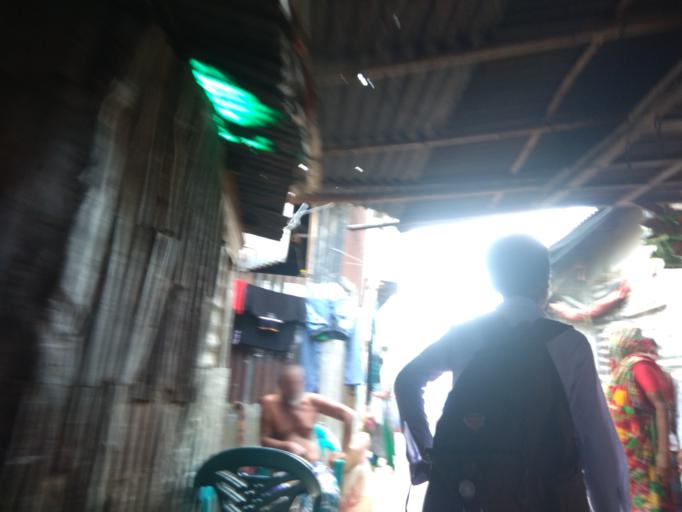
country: BD
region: Dhaka
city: Tungi
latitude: 23.8127
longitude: 90.3915
